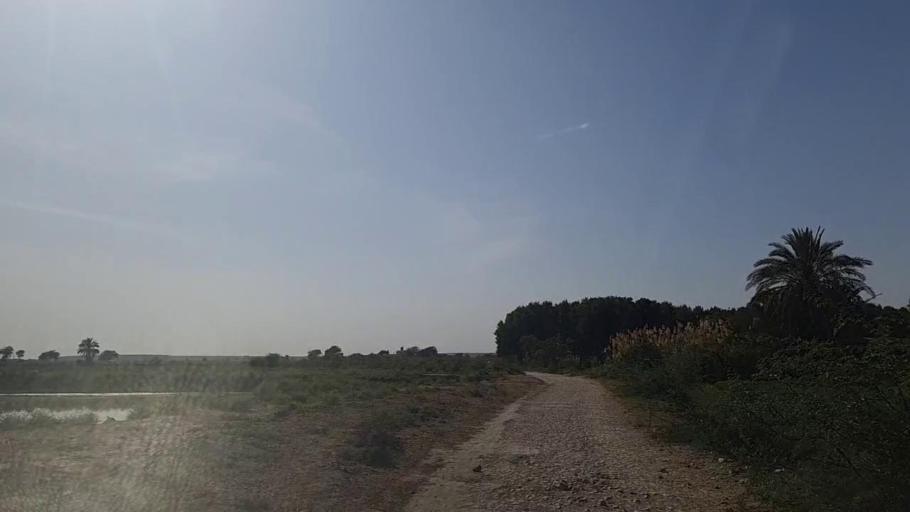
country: PK
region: Sindh
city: Thatta
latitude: 24.5910
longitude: 67.8928
